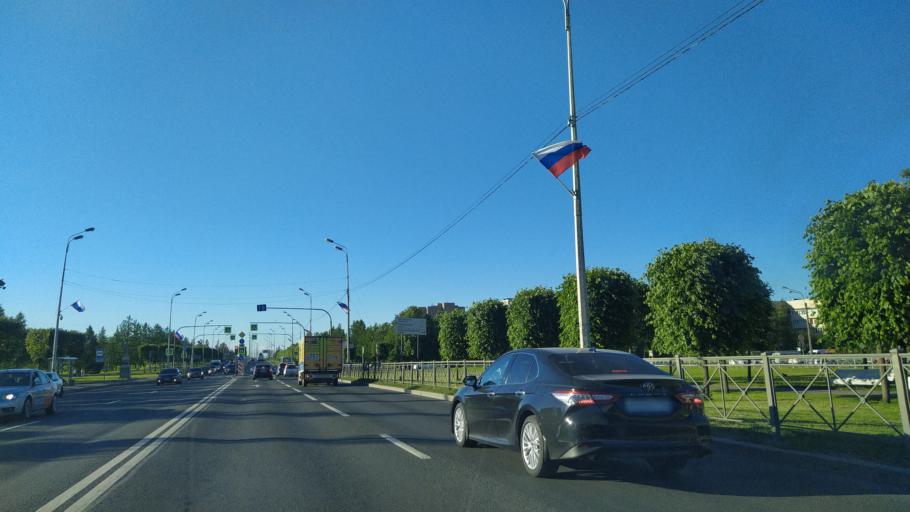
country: RU
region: St.-Petersburg
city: Pushkin
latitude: 59.7366
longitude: 30.3939
